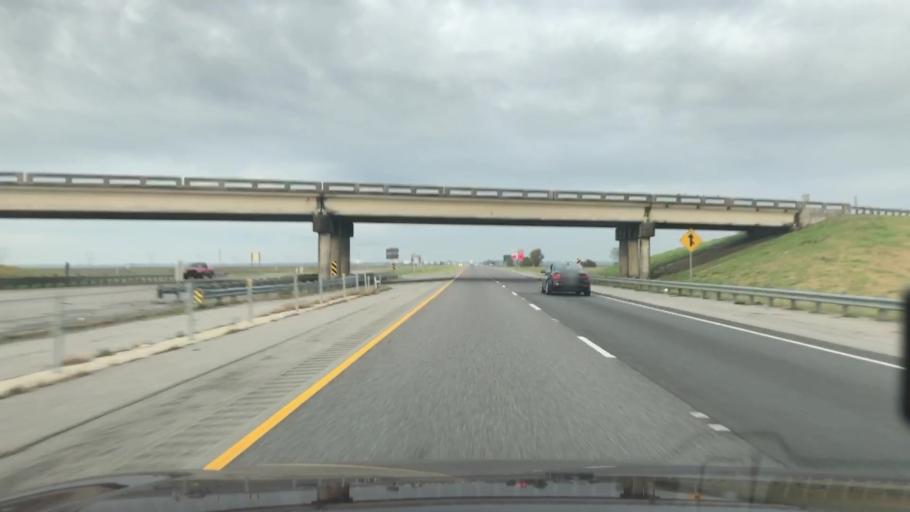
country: US
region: Mississippi
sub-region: Warren County
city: Vicksburg
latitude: 32.3216
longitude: -90.9595
